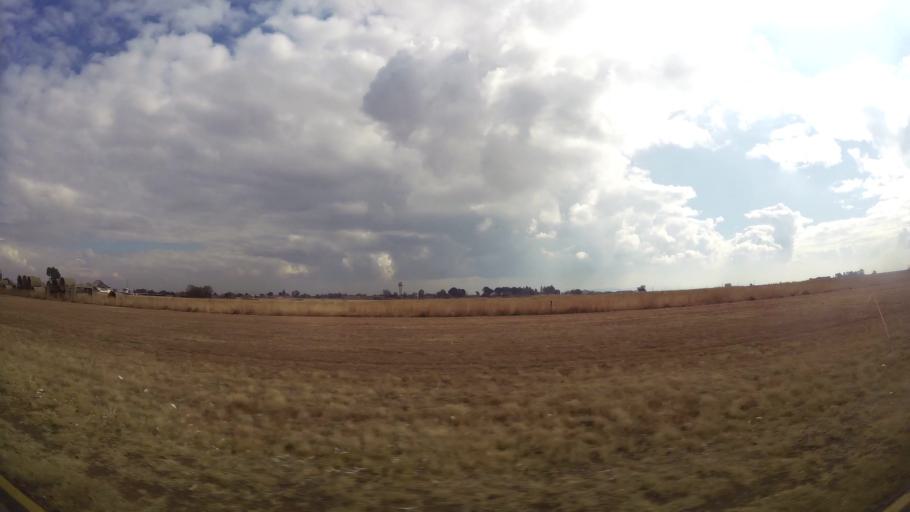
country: ZA
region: Gauteng
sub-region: Sedibeng District Municipality
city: Meyerton
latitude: -26.6141
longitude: 28.0644
